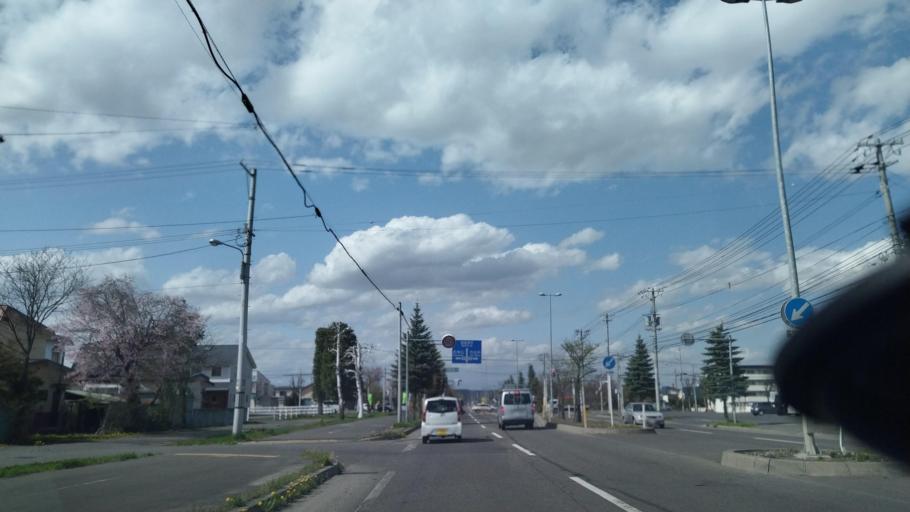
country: JP
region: Hokkaido
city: Obihiro
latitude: 42.9190
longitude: 143.1442
